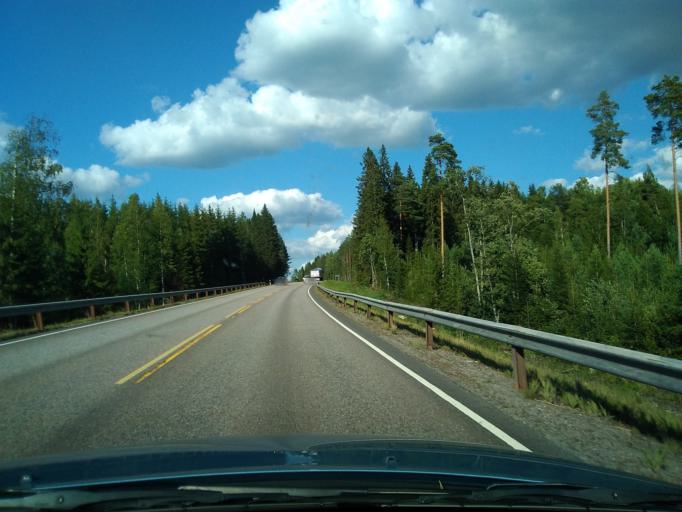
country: FI
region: Pirkanmaa
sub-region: Ylae-Pirkanmaa
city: Maenttae
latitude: 62.0994
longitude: 24.7314
